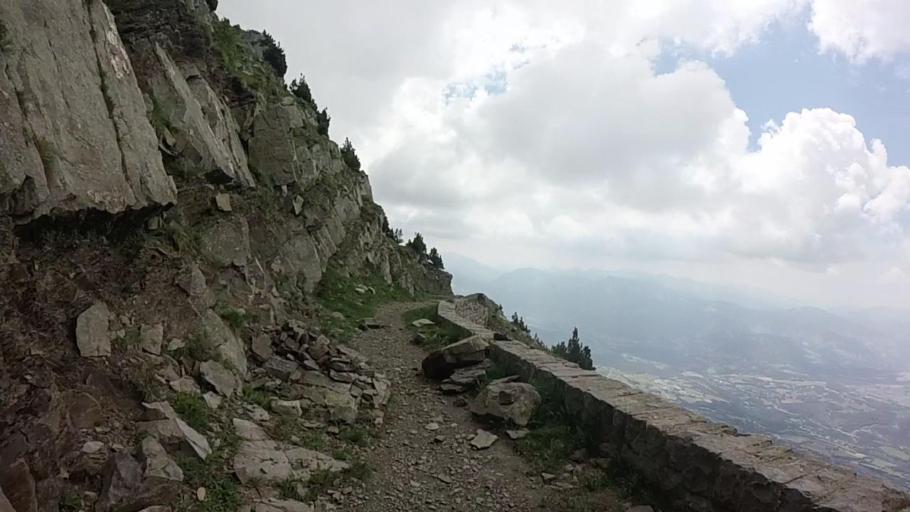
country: FR
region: Provence-Alpes-Cote d'Azur
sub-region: Departement des Alpes-de-Haute-Provence
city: Seyne-les-Alpes
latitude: 44.4086
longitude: 6.3818
